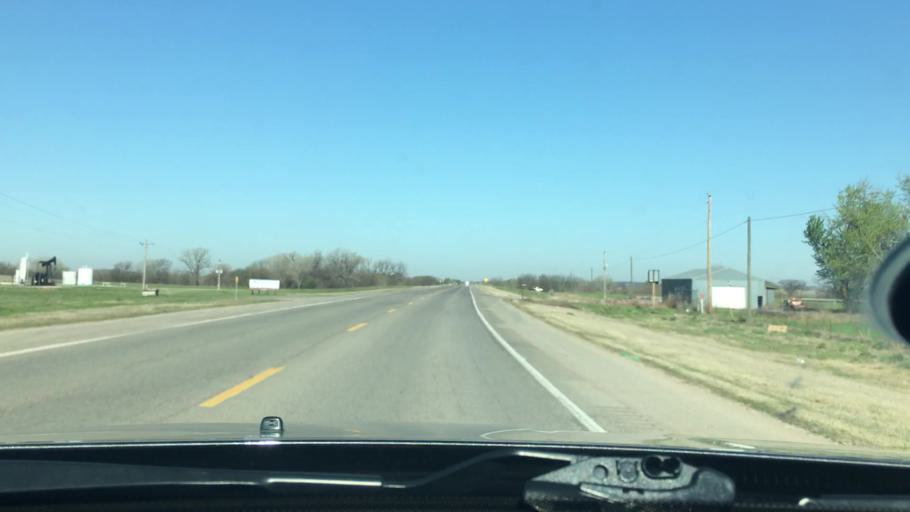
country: US
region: Oklahoma
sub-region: Garvin County
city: Lindsay
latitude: 34.8288
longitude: -97.5676
